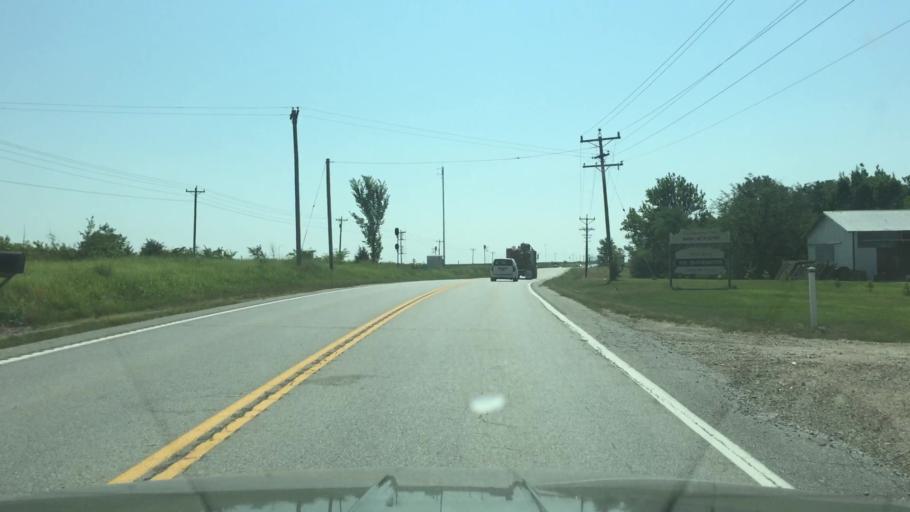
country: US
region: Missouri
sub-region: Moniteau County
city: Tipton
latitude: 38.6718
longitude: -92.8539
